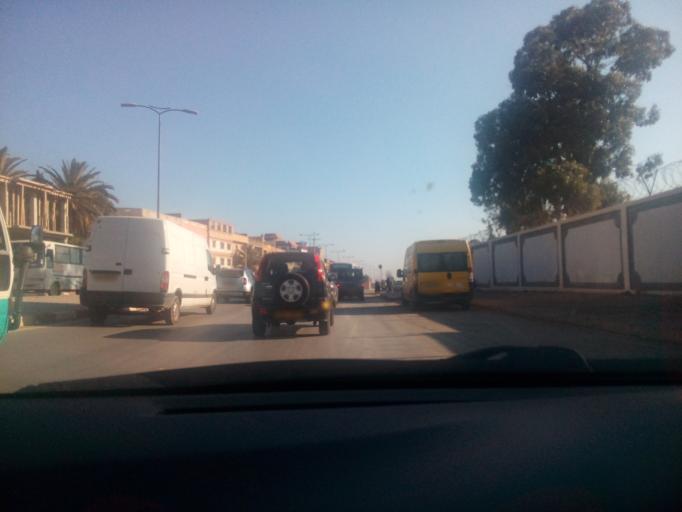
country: DZ
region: Oran
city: Oran
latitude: 35.6607
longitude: -0.6933
